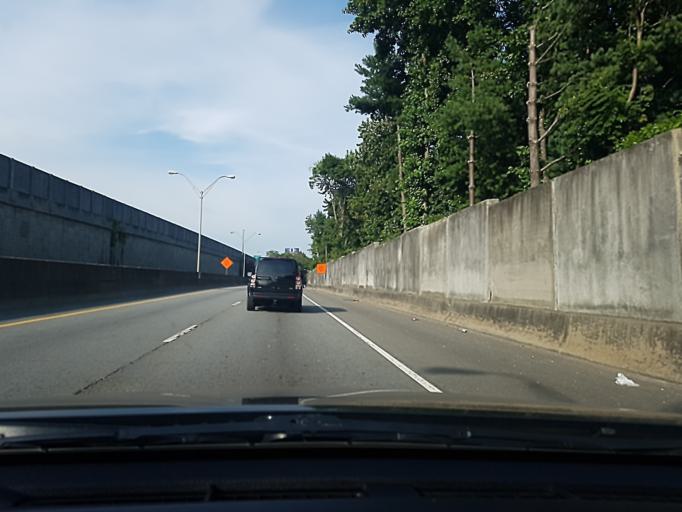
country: US
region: Georgia
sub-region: DeKalb County
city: Druid Hills
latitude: 33.8040
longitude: -84.3834
